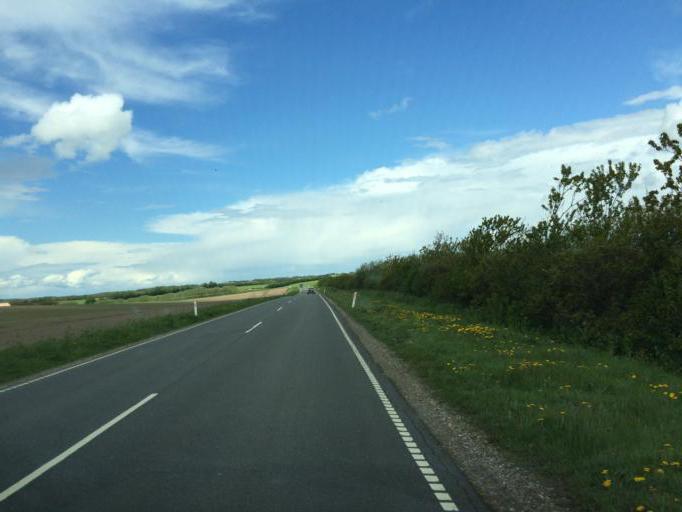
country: DK
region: North Denmark
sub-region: Vesthimmerland Kommune
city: Farso
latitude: 56.8021
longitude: 9.3523
